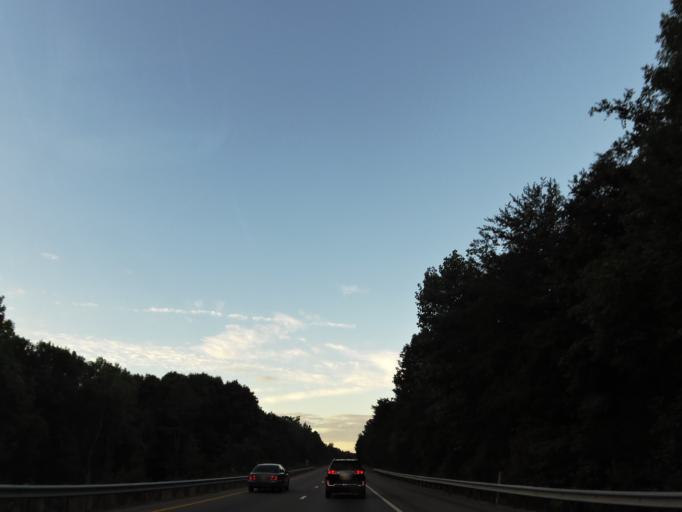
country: US
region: Tennessee
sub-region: Meigs County
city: Decatur
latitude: 35.3813
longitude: -84.7278
